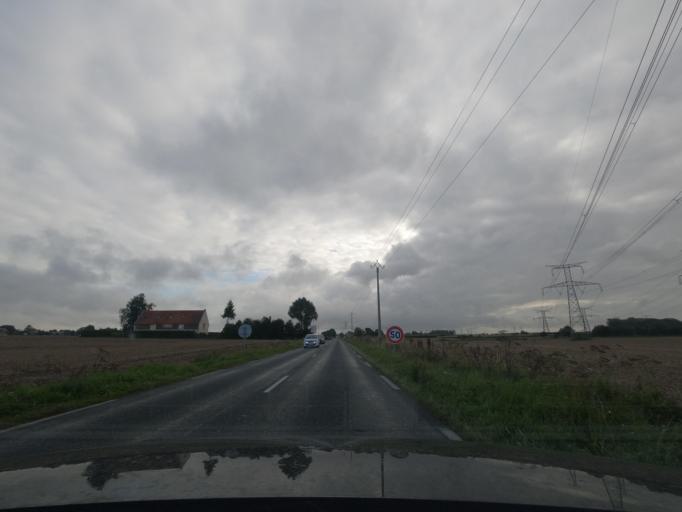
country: FR
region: Haute-Normandie
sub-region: Departement de la Seine-Maritime
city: Saint-Martin-Osmonville
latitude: 49.5781
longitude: 1.2907
